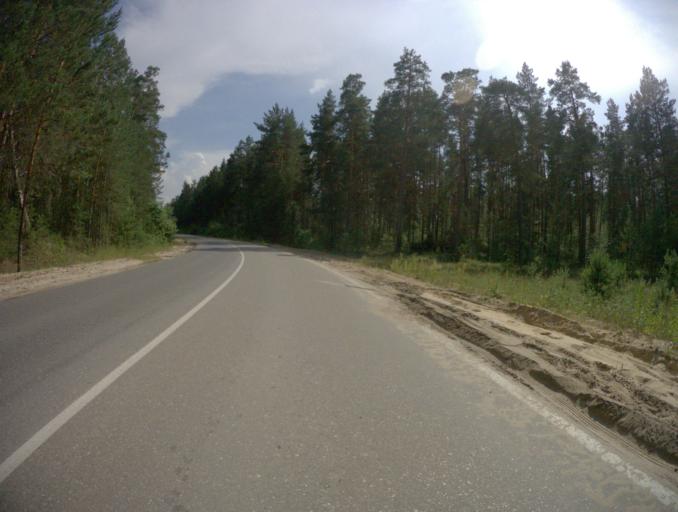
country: RU
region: Vladimir
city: Gorokhovets
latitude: 56.3031
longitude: 42.7738
